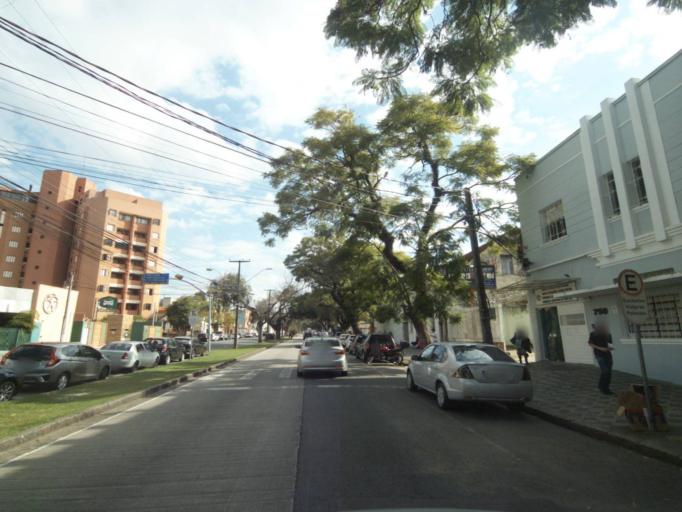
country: BR
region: Parana
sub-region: Curitiba
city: Curitiba
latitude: -25.4420
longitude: -49.2690
